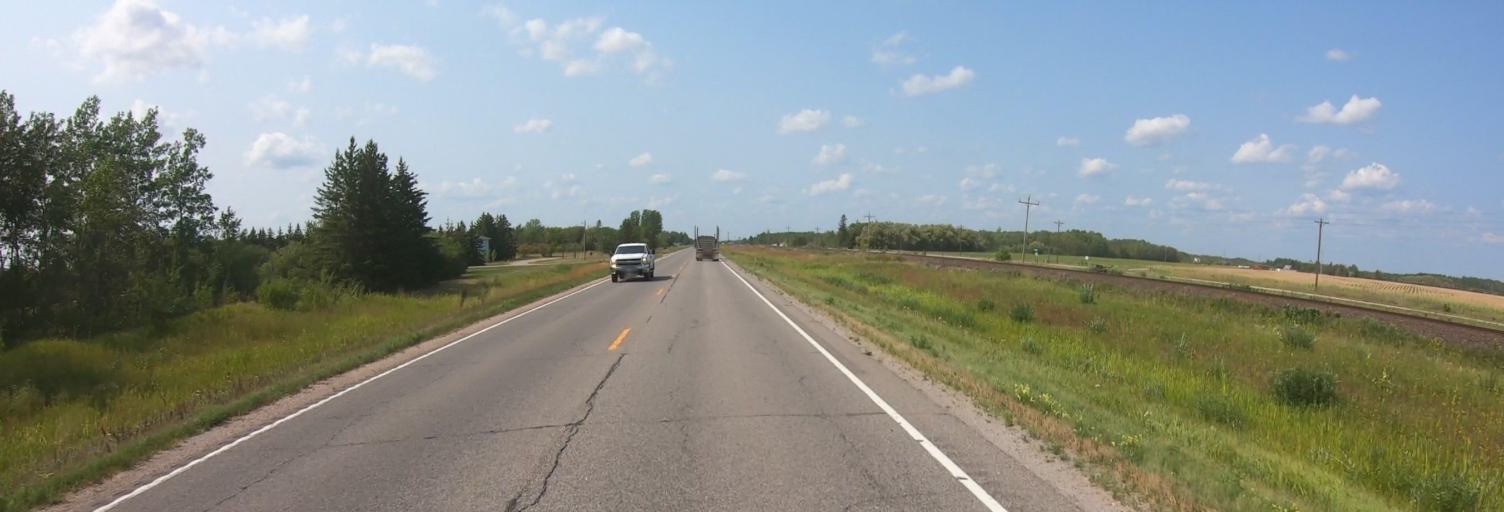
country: US
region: Minnesota
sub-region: Roseau County
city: Warroad
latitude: 48.8834
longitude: -95.2918
